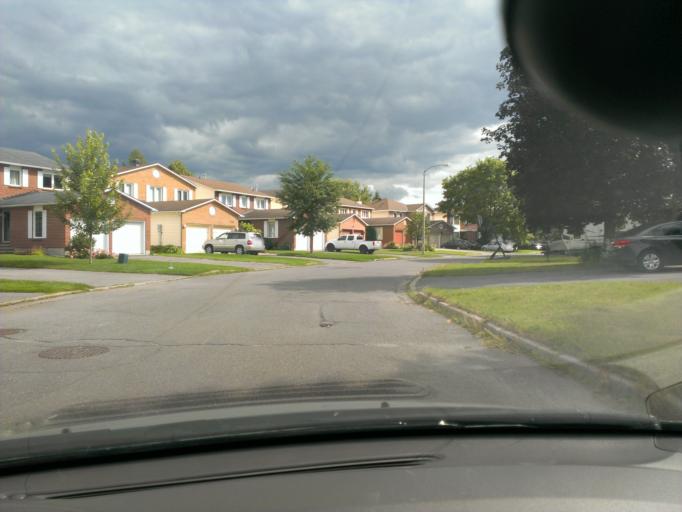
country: CA
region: Quebec
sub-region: Outaouais
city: Gatineau
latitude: 45.4813
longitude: -75.4912
